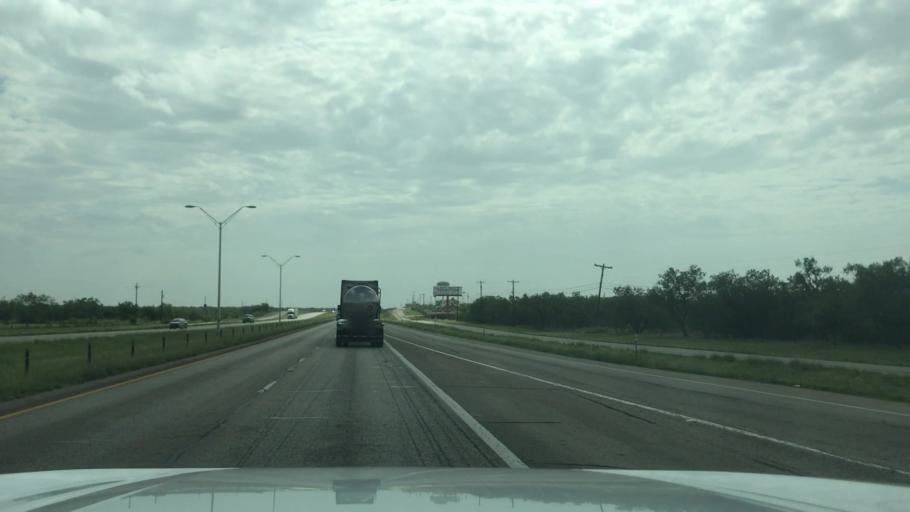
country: US
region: Texas
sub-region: Callahan County
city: Clyde
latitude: 32.4315
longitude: -99.6017
